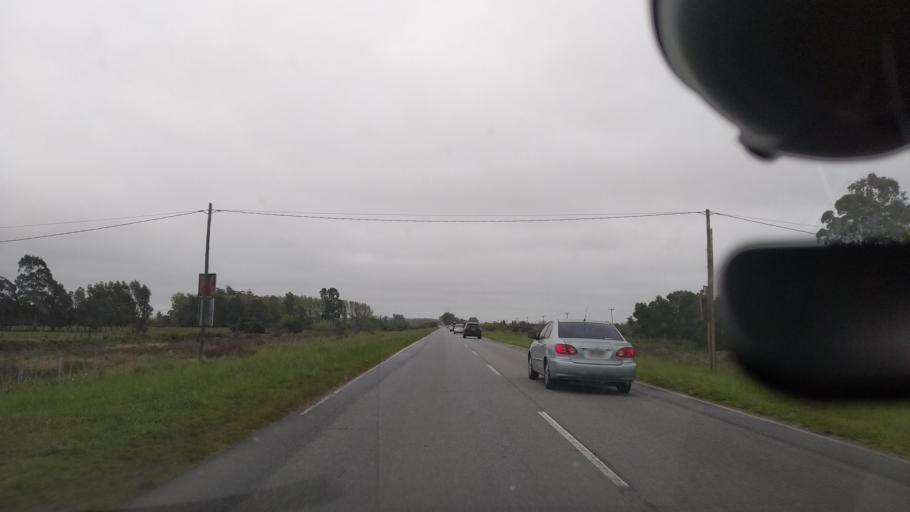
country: AR
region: Buenos Aires
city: Veronica
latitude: -35.3955
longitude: -57.3572
